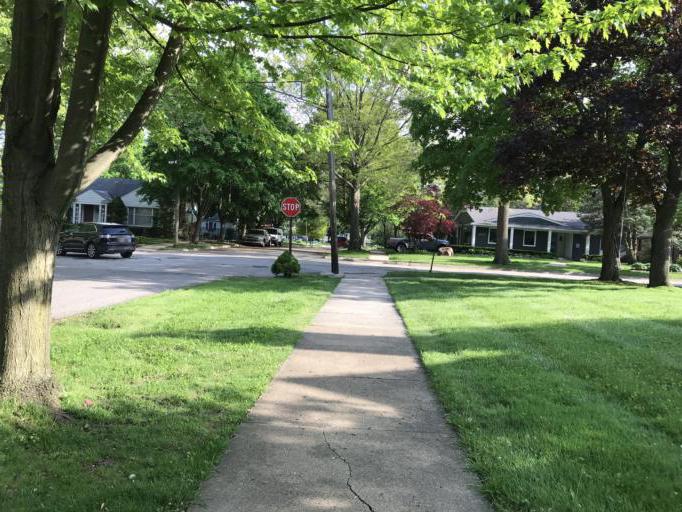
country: US
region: Michigan
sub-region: Oakland County
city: Farmington
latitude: 42.4642
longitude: -83.3800
